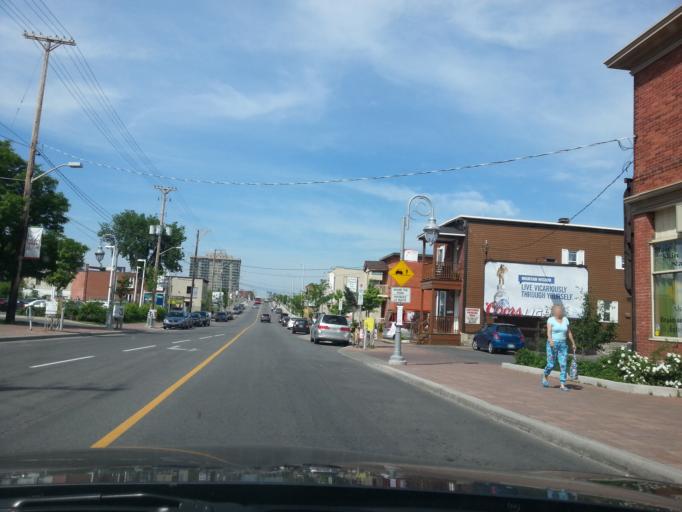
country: CA
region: Ontario
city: Ottawa
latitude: 45.4083
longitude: -75.7144
